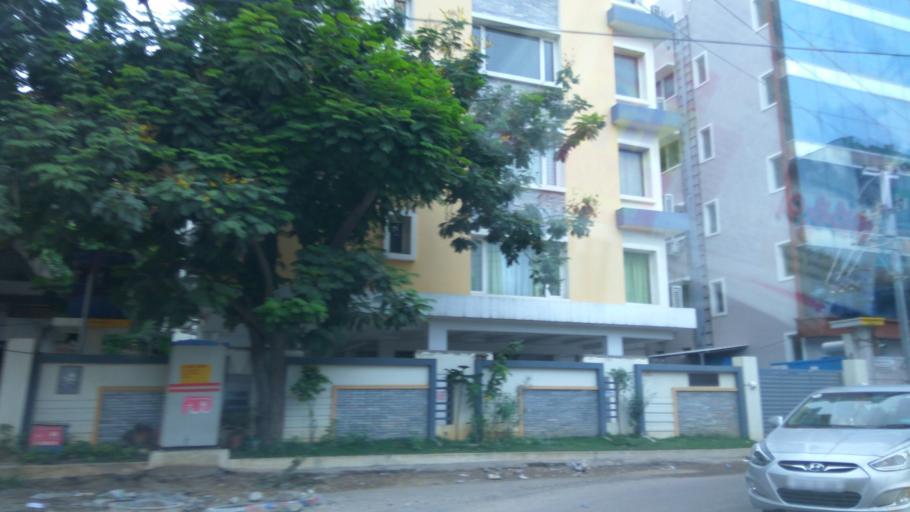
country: IN
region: Telangana
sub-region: Rangareddi
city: Kukatpalli
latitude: 17.4378
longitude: 78.3874
